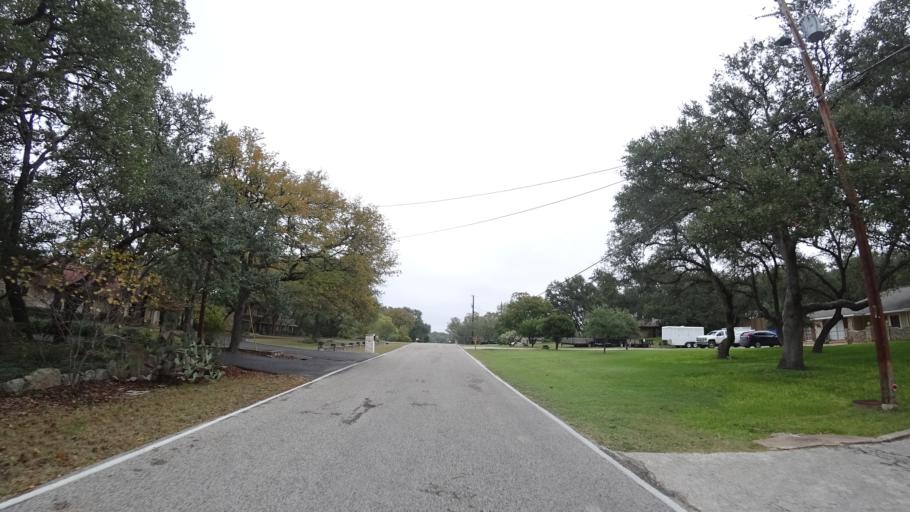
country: US
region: Texas
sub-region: Travis County
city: Shady Hollow
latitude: 30.2229
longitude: -97.8980
